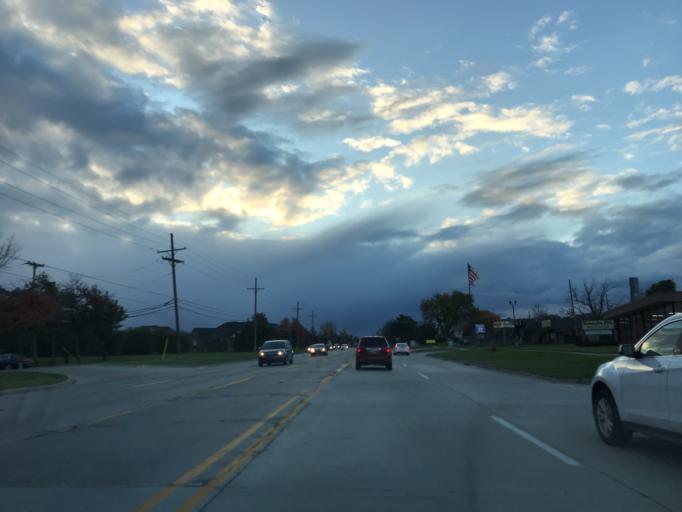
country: US
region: Michigan
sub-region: Oakland County
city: Farmington
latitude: 42.4403
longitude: -83.3856
